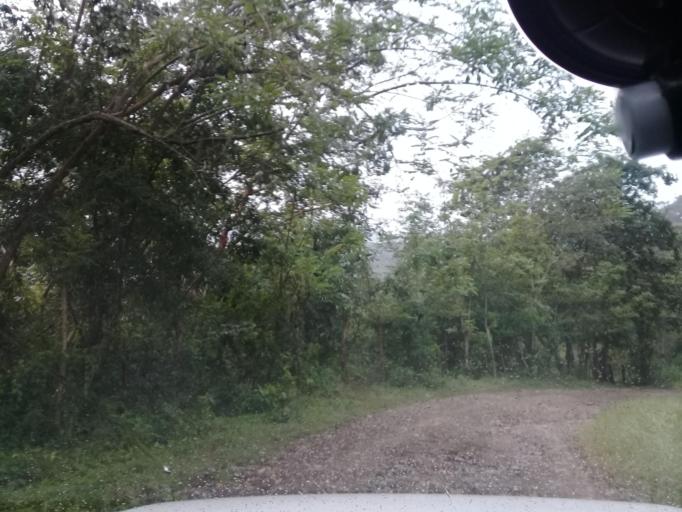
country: MX
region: Veracruz
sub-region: Chalma
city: San Pedro Coyutla
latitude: 21.2445
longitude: -98.4185
